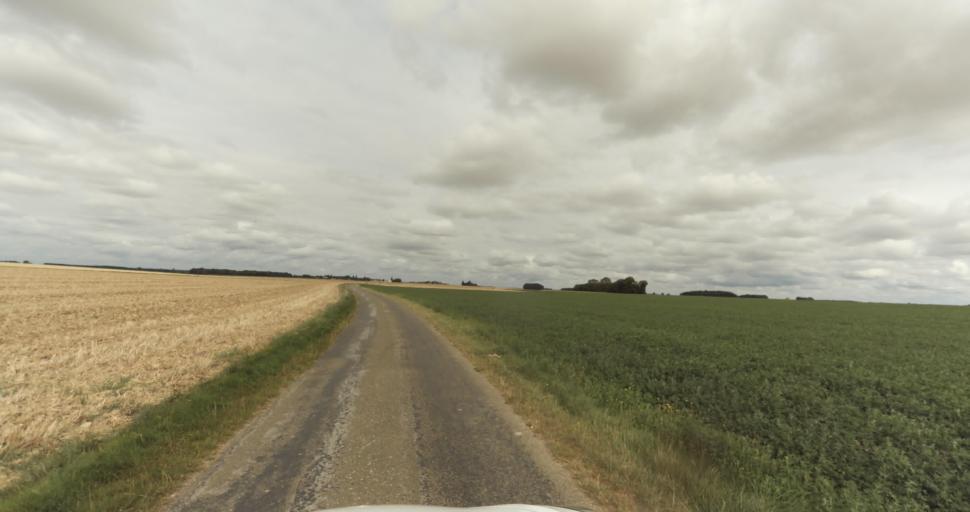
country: FR
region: Haute-Normandie
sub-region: Departement de l'Eure
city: Tillieres-sur-Avre
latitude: 48.7773
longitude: 1.0808
